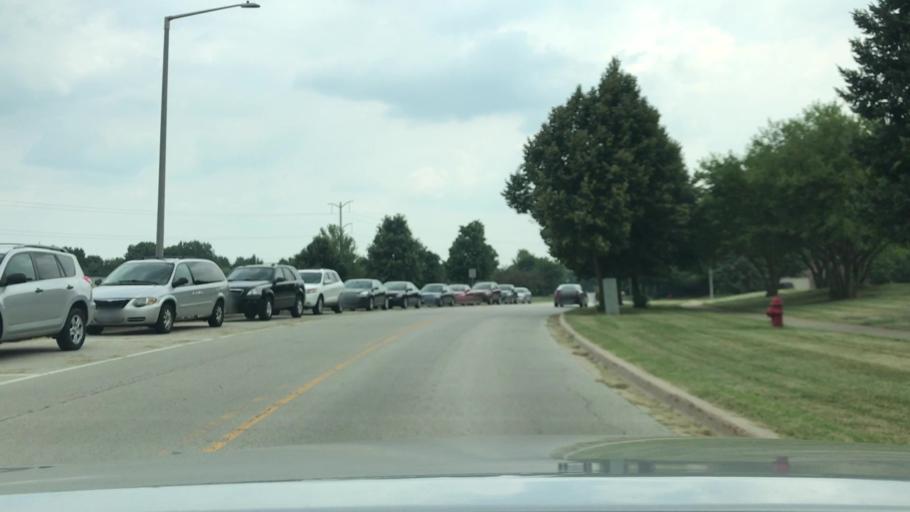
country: US
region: Illinois
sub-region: Will County
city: Plainfield
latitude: 41.6067
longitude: -88.2150
